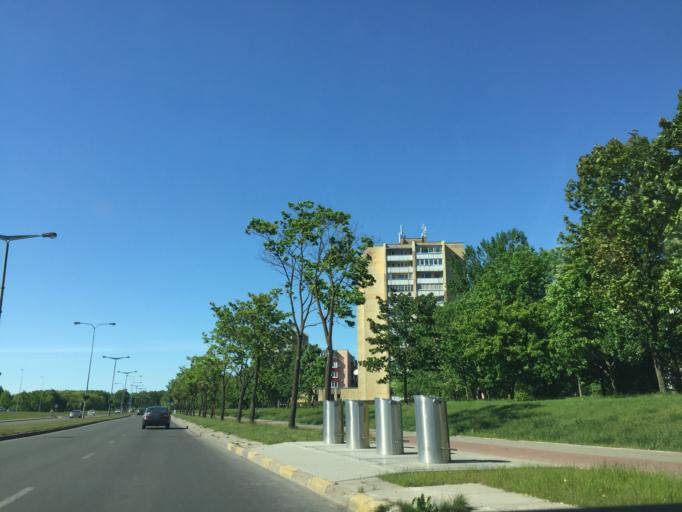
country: LT
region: Panevezys
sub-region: Panevezys City
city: Panevezys
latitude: 55.7335
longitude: 24.3410
